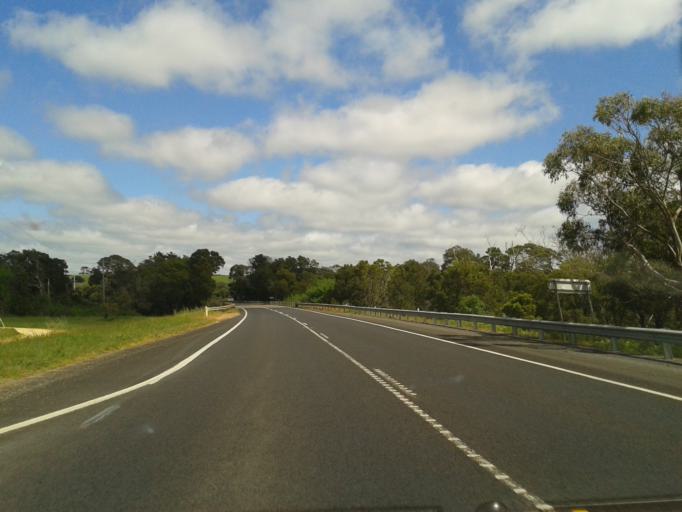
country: AU
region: Victoria
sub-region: Glenelg
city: Portland
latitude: -38.2199
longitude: 141.7649
